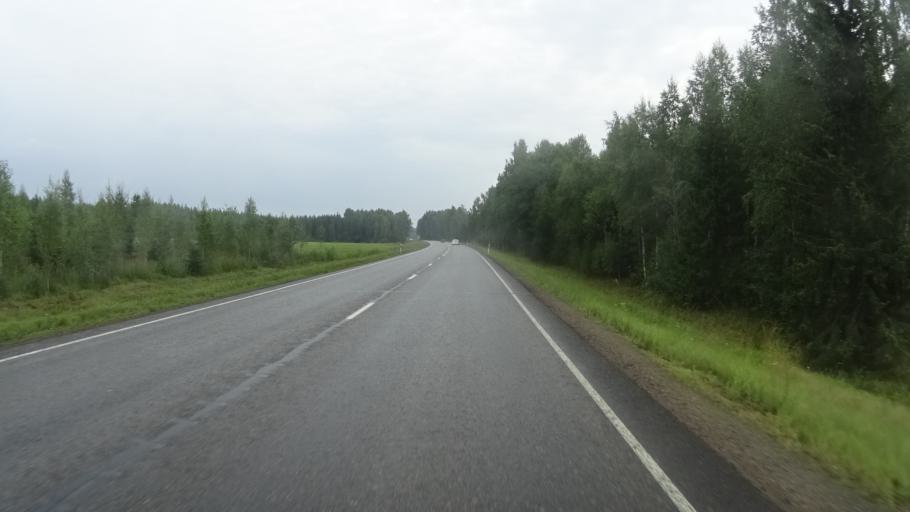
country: FI
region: Kymenlaakso
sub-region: Kouvola
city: Anjala
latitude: 60.7989
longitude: 26.8025
